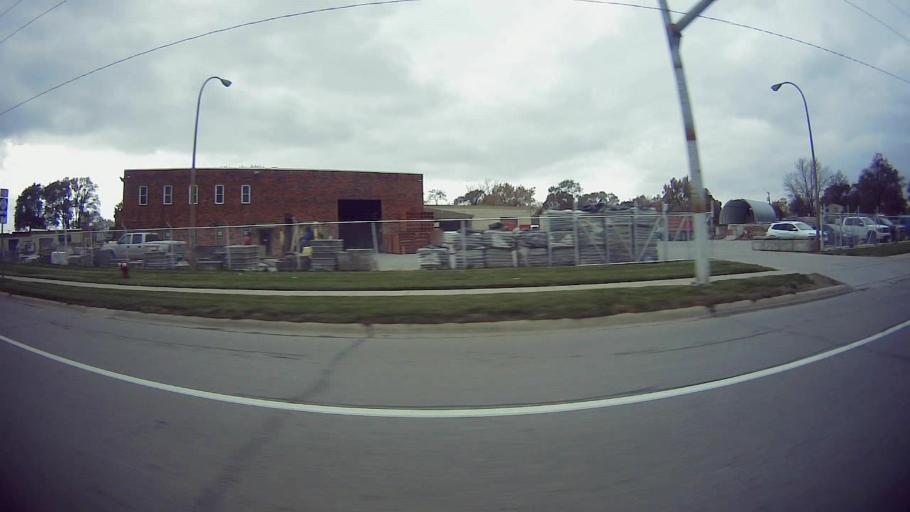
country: US
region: Michigan
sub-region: Macomb County
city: Warren
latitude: 42.4499
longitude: -83.0064
